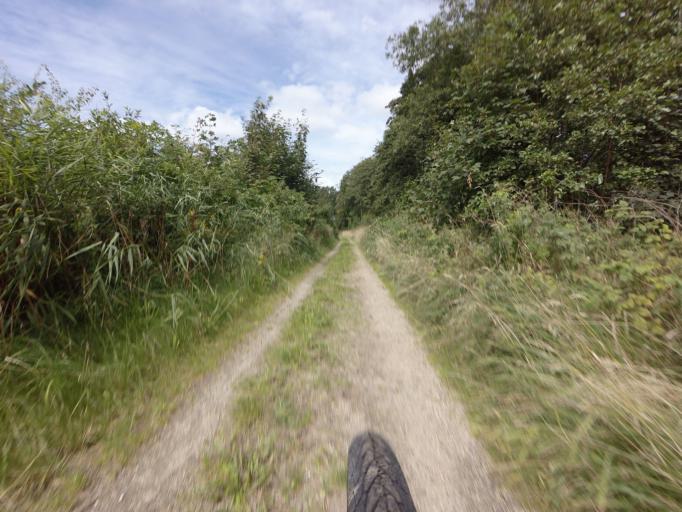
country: DK
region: Central Jutland
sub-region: Syddjurs Kommune
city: Ryomgard
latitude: 56.3852
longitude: 10.5336
